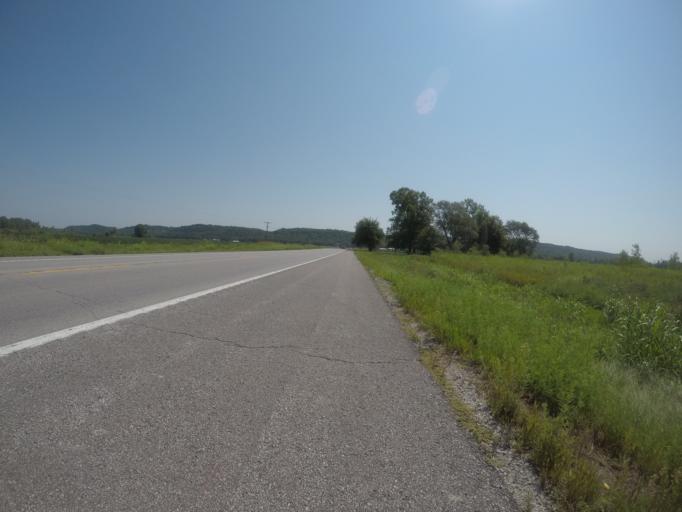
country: US
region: Kansas
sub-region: Atchison County
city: Atchison
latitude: 39.5566
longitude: -95.0579
